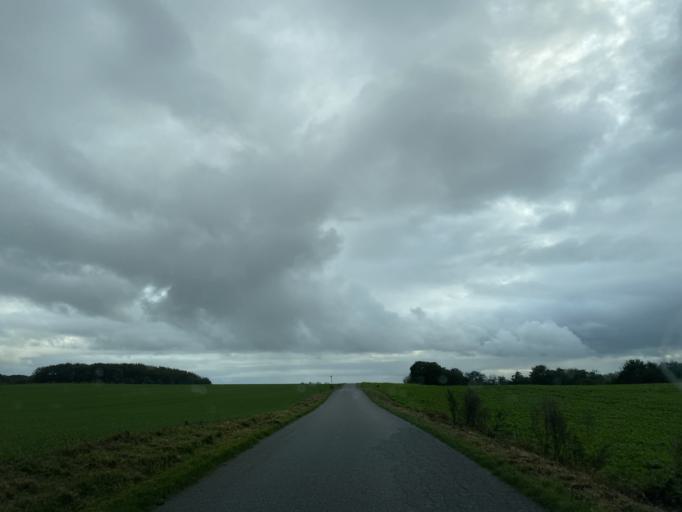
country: DK
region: Central Jutland
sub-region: Viborg Kommune
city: Bjerringbro
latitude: 56.3444
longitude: 9.7146
